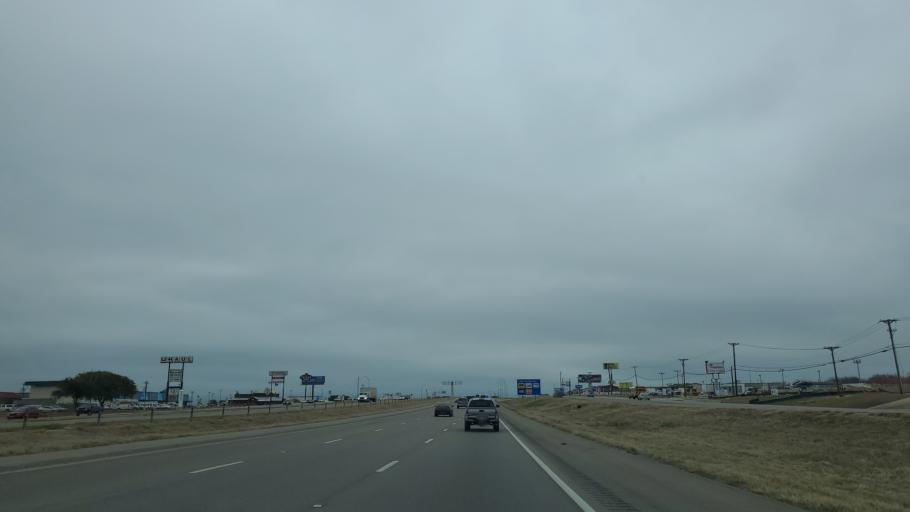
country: US
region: Texas
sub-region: Bell County
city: Killeen
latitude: 31.0839
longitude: -97.7060
